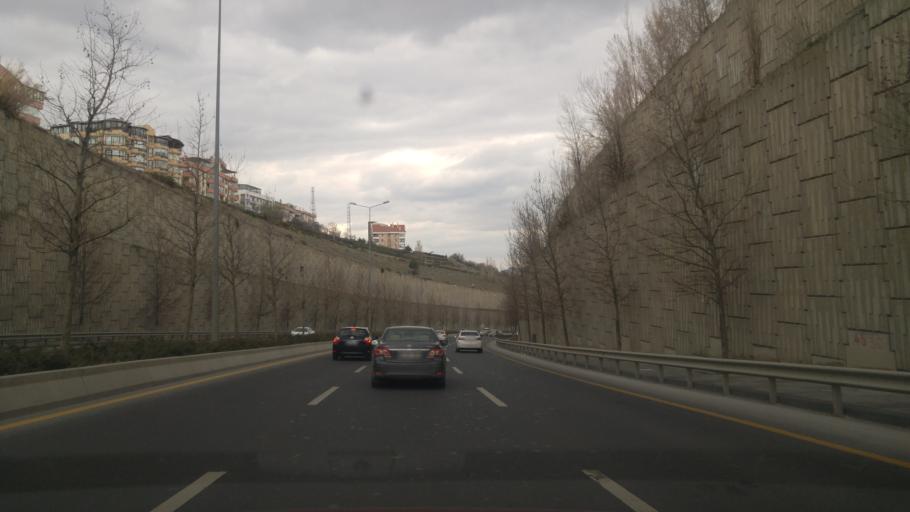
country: TR
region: Ankara
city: Cankaya
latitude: 39.8851
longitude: 32.8895
